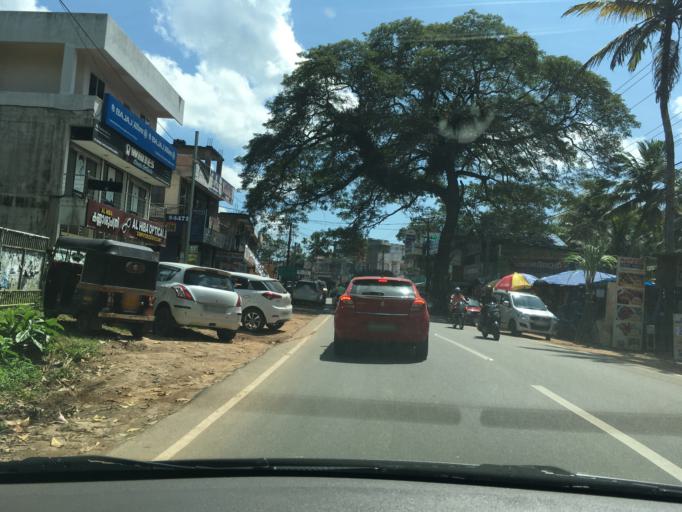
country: IN
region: Kerala
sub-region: Thiruvananthapuram
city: Nedumangad
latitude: 8.6023
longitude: 76.9962
